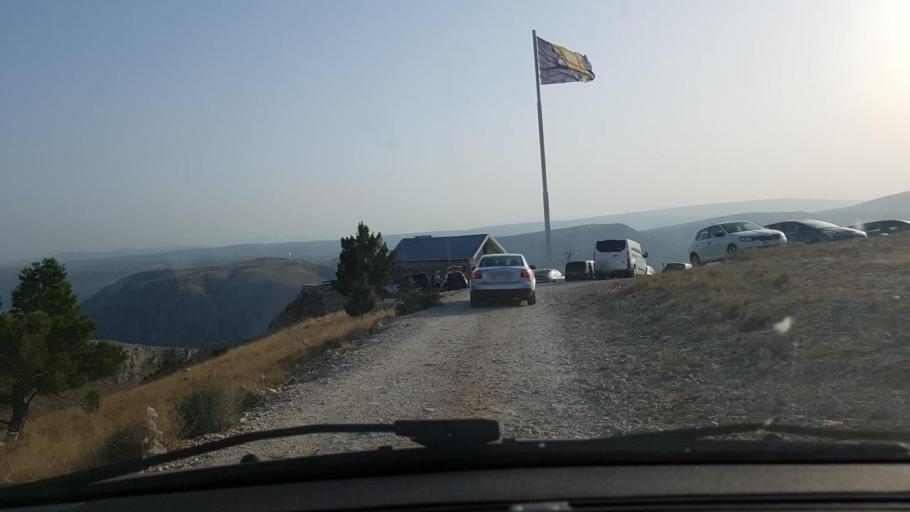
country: BA
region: Federation of Bosnia and Herzegovina
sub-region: Hercegovacko-Bosanski Kanton
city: Mostar
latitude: 43.3503
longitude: 17.8316
